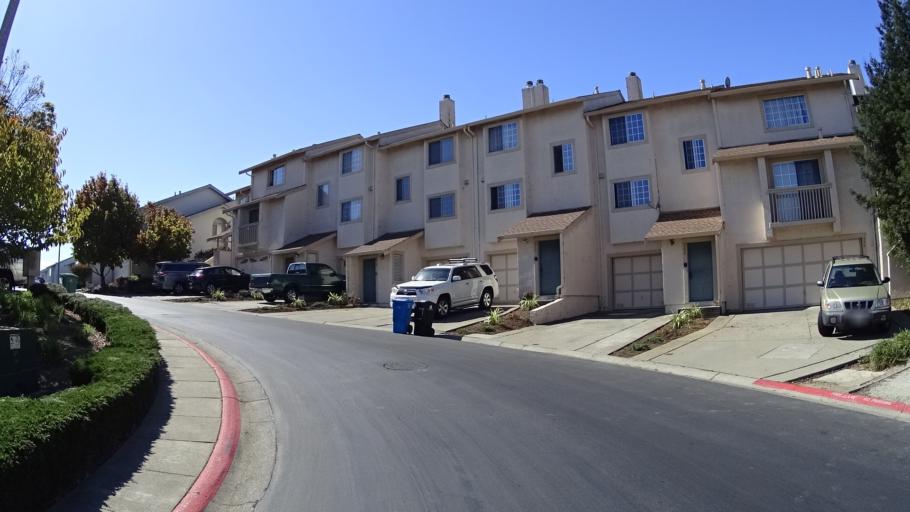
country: US
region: California
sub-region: San Francisco County
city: San Francisco
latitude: 37.7344
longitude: -122.3966
